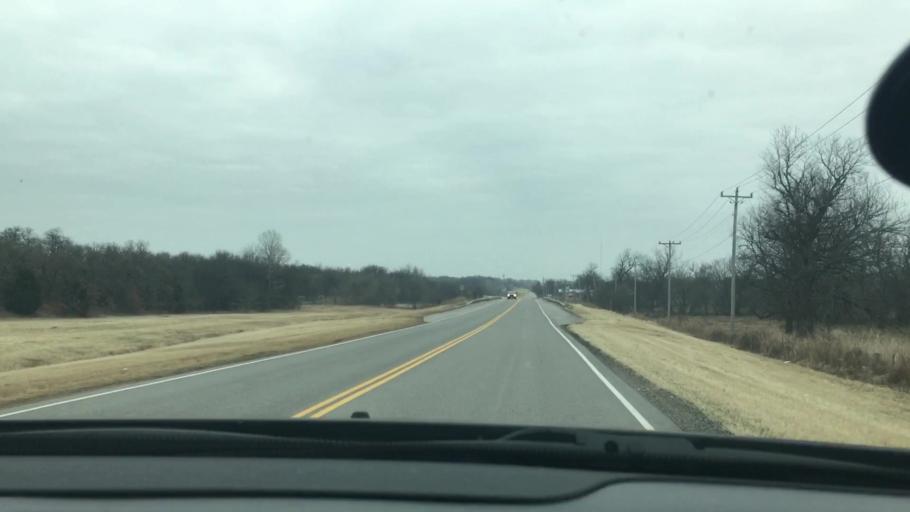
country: US
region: Oklahoma
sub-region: Carter County
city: Healdton
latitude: 34.2491
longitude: -97.4923
